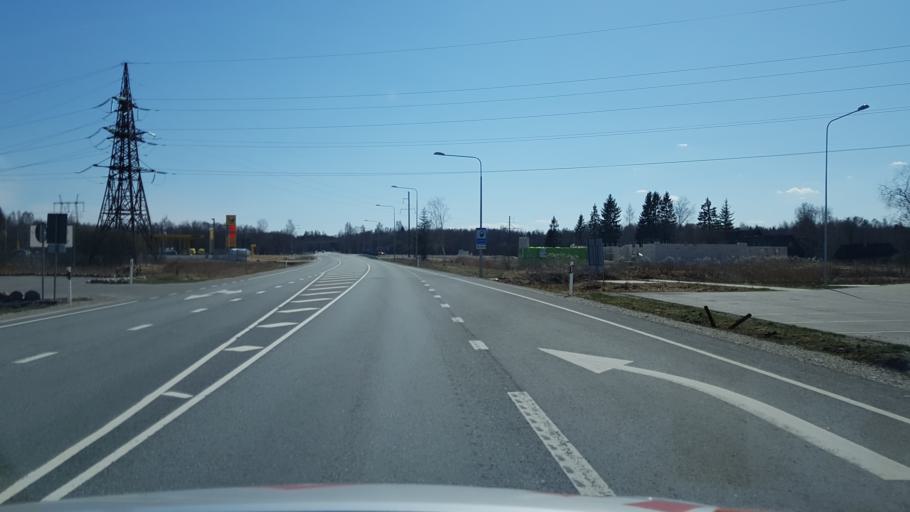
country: EE
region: Jogevamaa
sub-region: Mustvee linn
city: Mustvee
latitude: 58.8500
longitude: 26.9135
